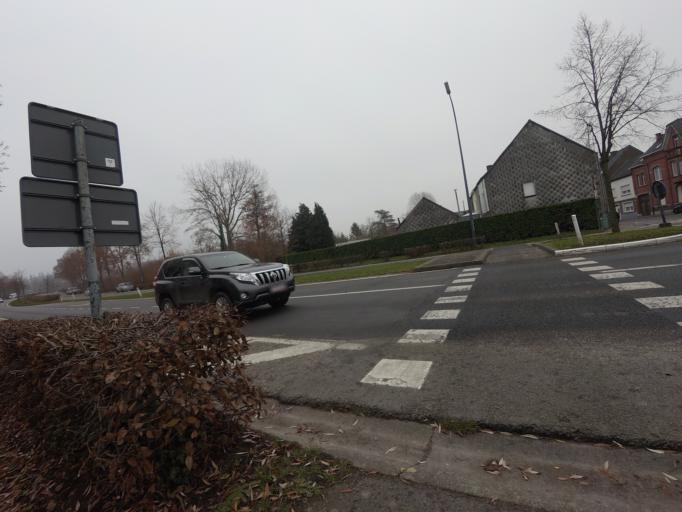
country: BE
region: Flanders
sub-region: Provincie Oost-Vlaanderen
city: Geraardsbergen
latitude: 50.7782
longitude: 3.8757
